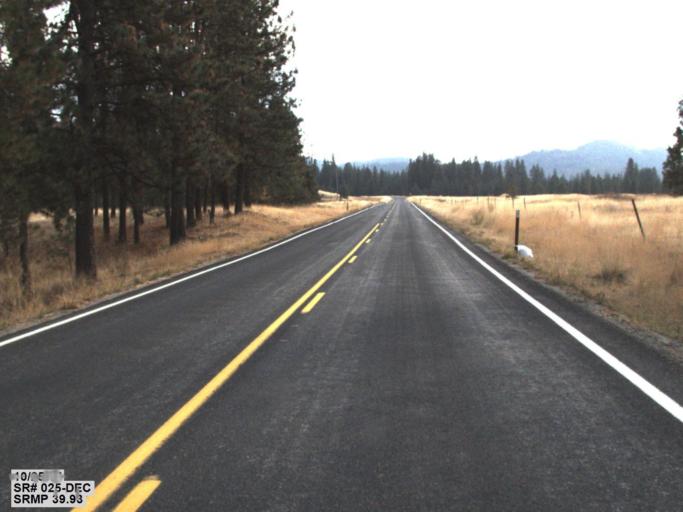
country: US
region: Washington
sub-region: Lincoln County
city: Davenport
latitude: 48.0963
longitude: -118.2018
